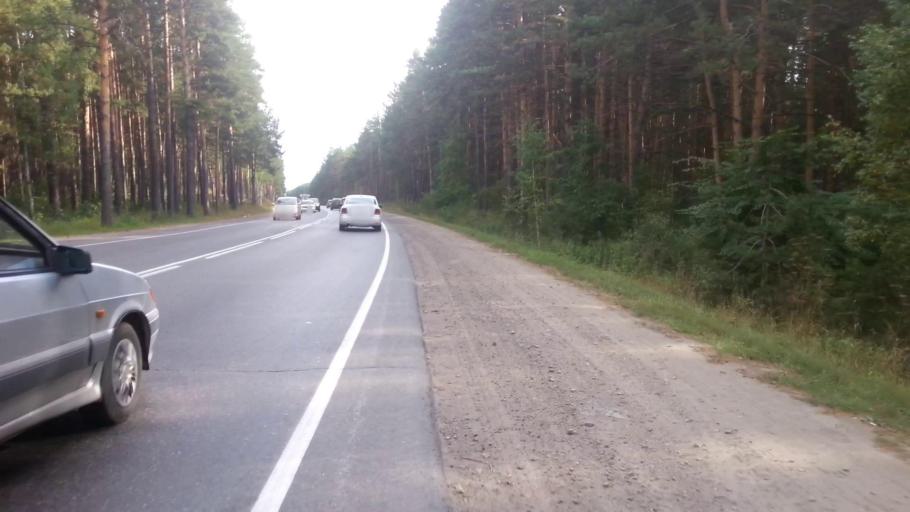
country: RU
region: Altai Krai
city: Yuzhnyy
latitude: 53.2982
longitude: 83.7029
